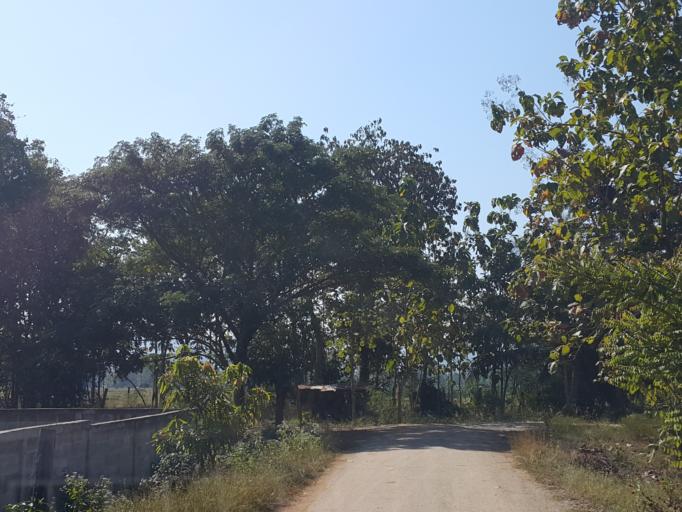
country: TH
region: Sukhothai
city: Thung Saliam
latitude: 17.3414
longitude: 99.4448
